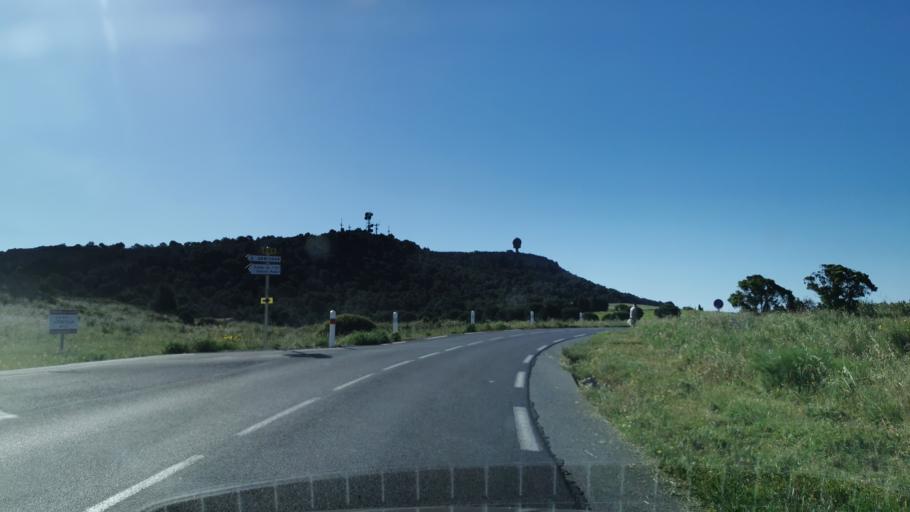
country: FR
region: Languedoc-Roussillon
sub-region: Departement de l'Aude
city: Armissan
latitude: 43.1766
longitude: 3.1073
